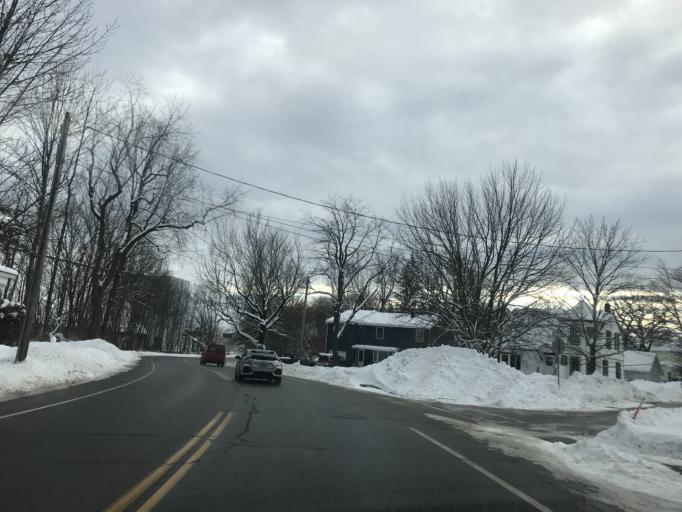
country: US
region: Maine
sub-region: Cumberland County
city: Westbrook
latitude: 43.6903
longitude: -70.3545
